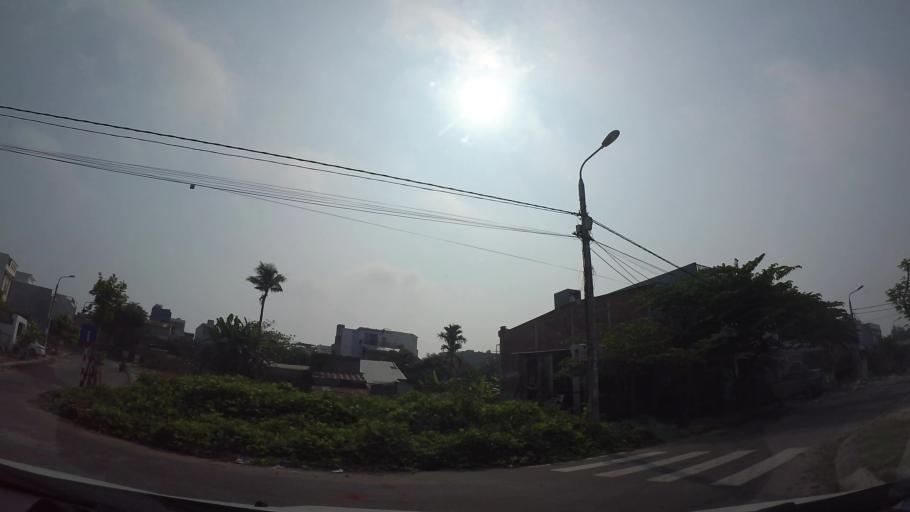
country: VN
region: Da Nang
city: Ngu Hanh Son
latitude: 16.0297
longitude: 108.2435
